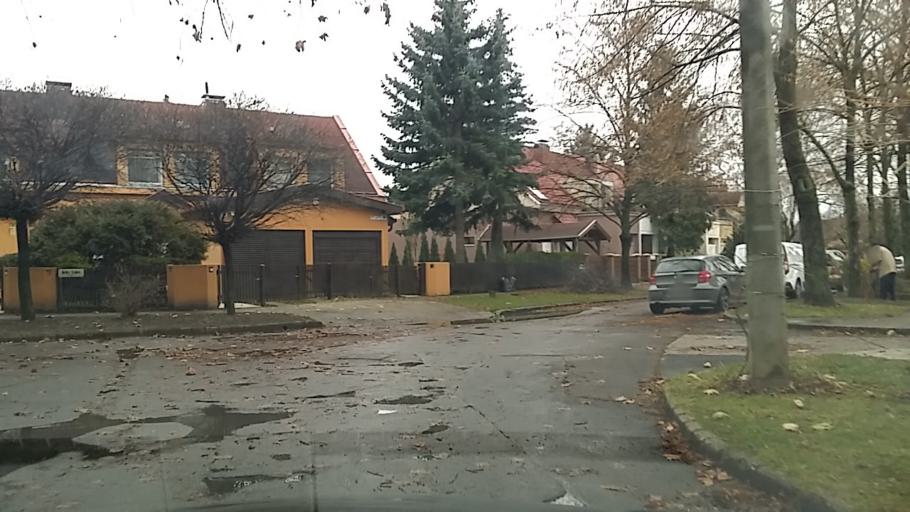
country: HU
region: Hajdu-Bihar
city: Debrecen
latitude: 47.5548
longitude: 21.6014
